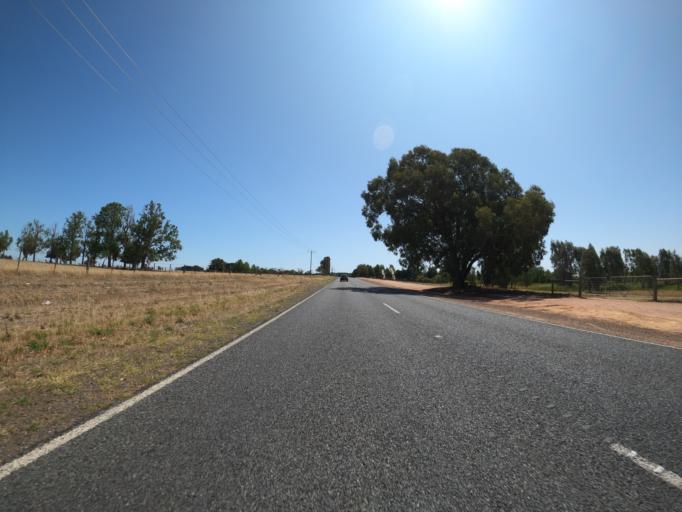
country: AU
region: Victoria
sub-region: Moira
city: Yarrawonga
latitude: -36.0272
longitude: 146.0798
